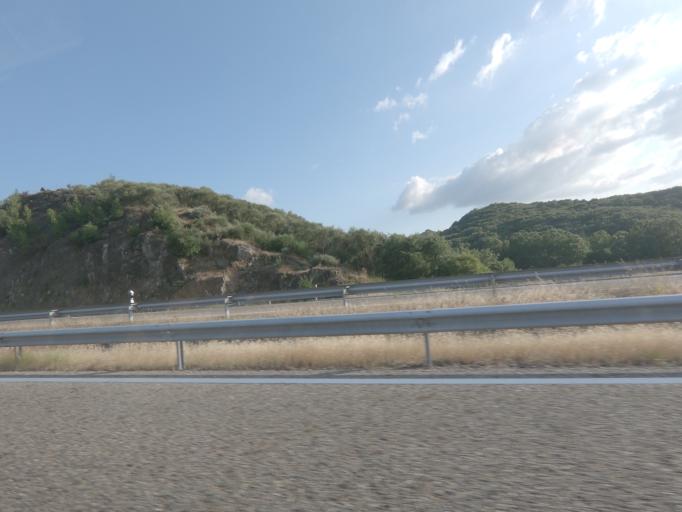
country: ES
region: Galicia
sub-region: Provincia de Ourense
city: Cualedro
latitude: 42.0085
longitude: -7.5686
